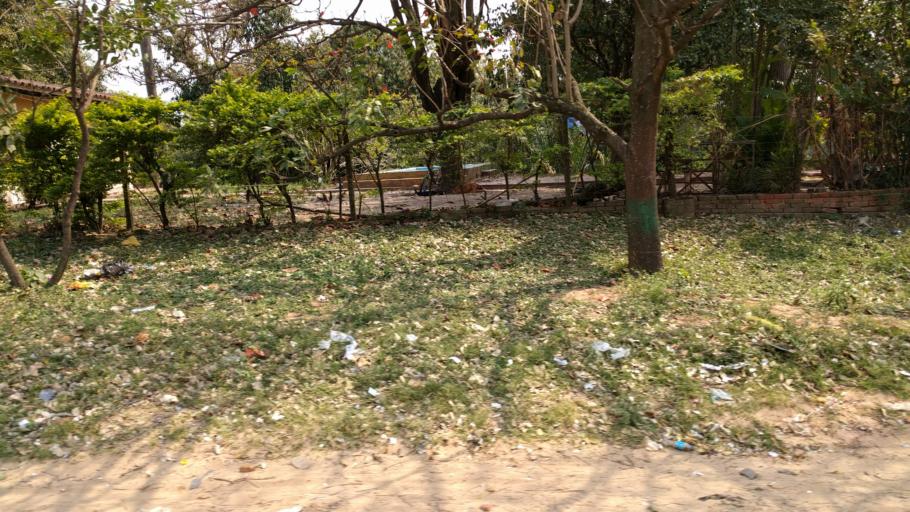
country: BO
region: Santa Cruz
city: Santa Rita
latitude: -17.9005
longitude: -63.3395
